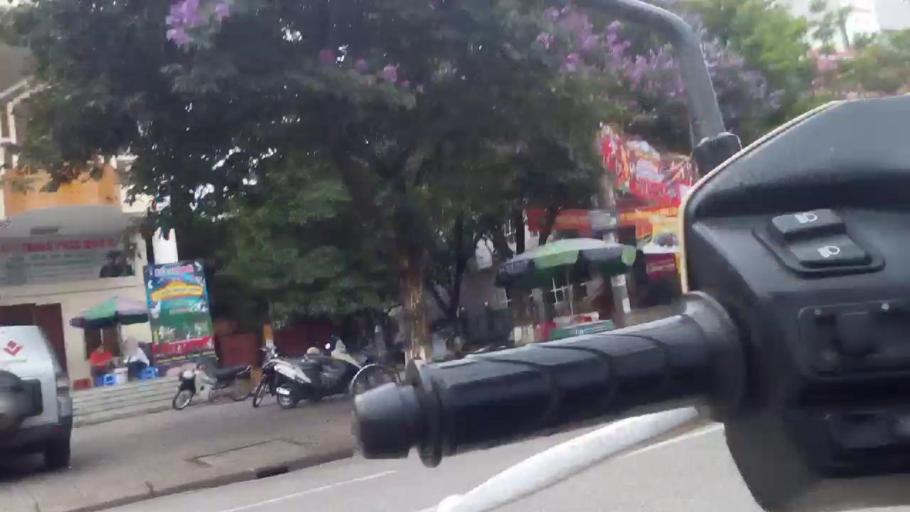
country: VN
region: Bac Giang
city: Bac Giang
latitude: 21.2773
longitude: 106.1923
